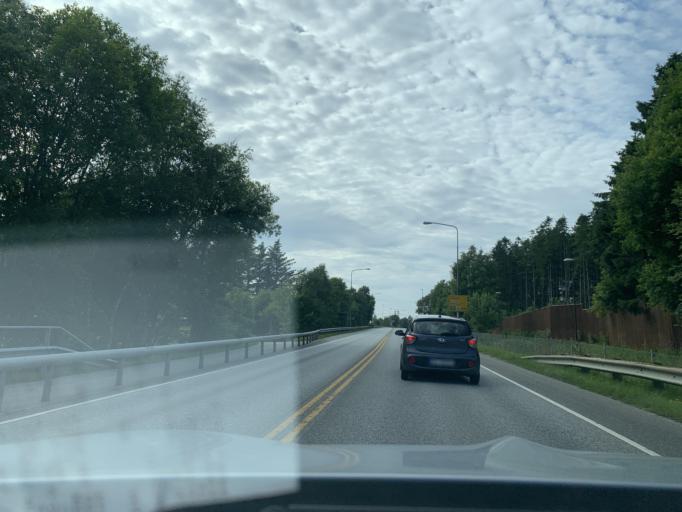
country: NO
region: Rogaland
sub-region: Stavanger
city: Stavanger
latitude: 58.9185
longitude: 5.7150
